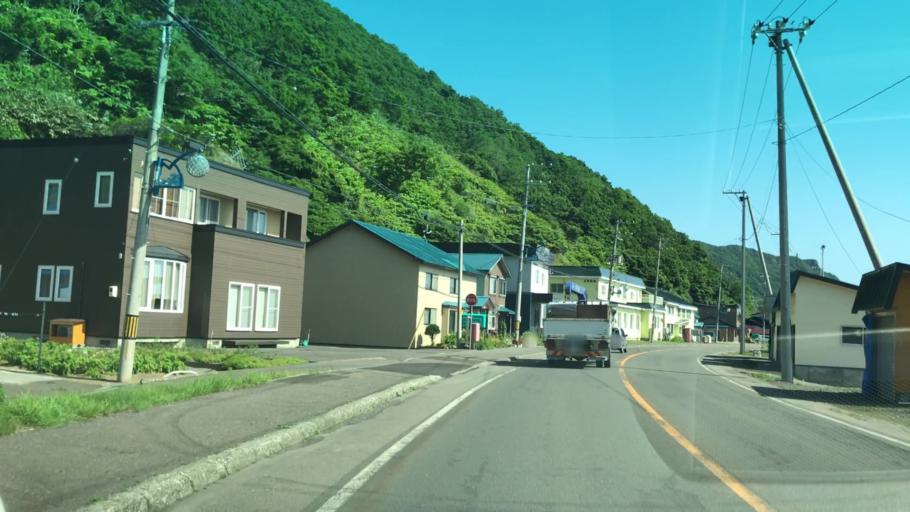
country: JP
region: Hokkaido
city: Iwanai
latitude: 43.1055
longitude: 140.4594
